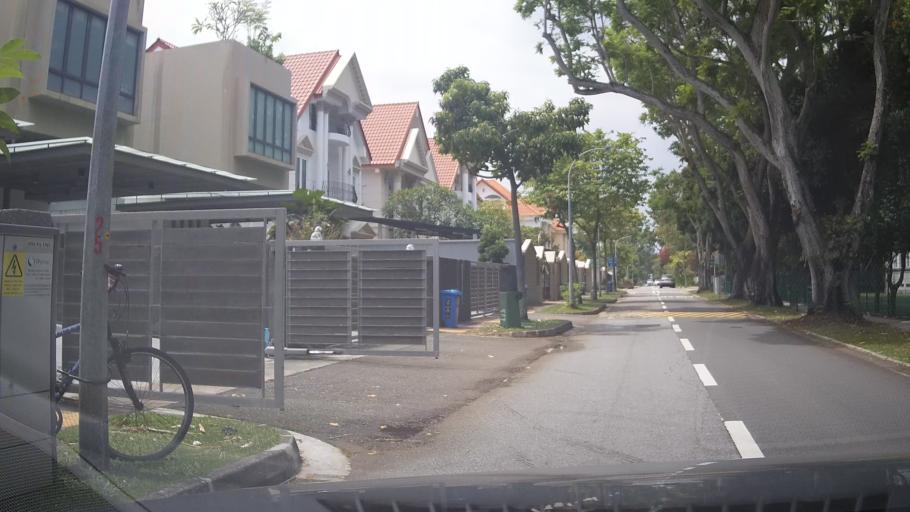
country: SG
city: Singapore
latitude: 1.3044
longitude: 103.8910
